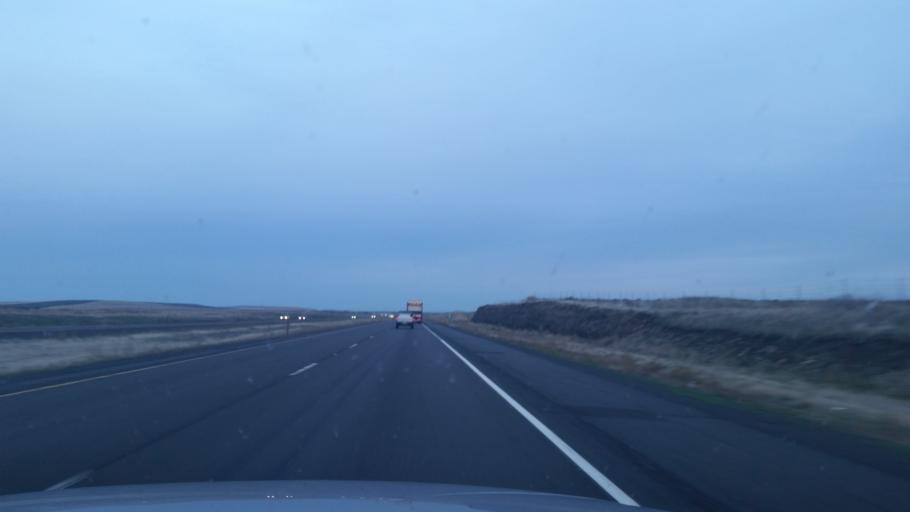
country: US
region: Washington
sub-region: Adams County
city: Ritzville
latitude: 47.2378
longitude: -118.1368
